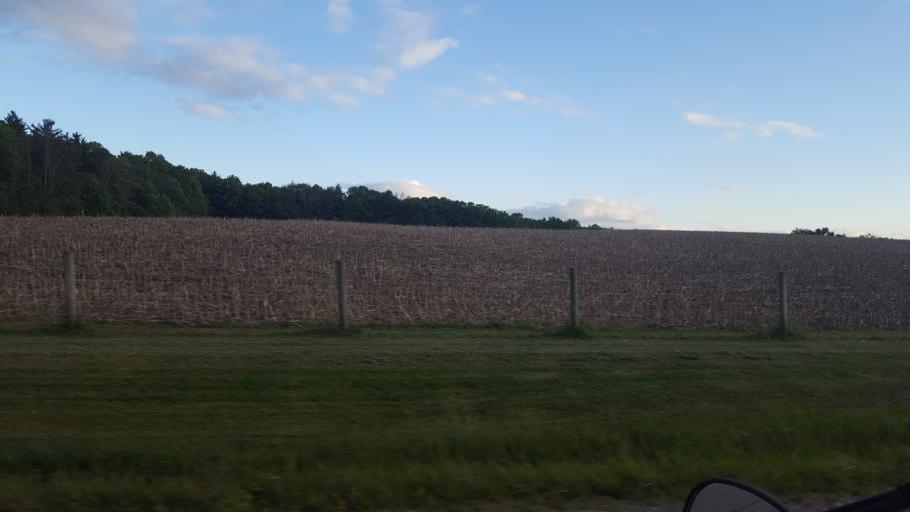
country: US
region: Ohio
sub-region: Knox County
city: Fredericktown
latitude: 40.4038
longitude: -82.6182
